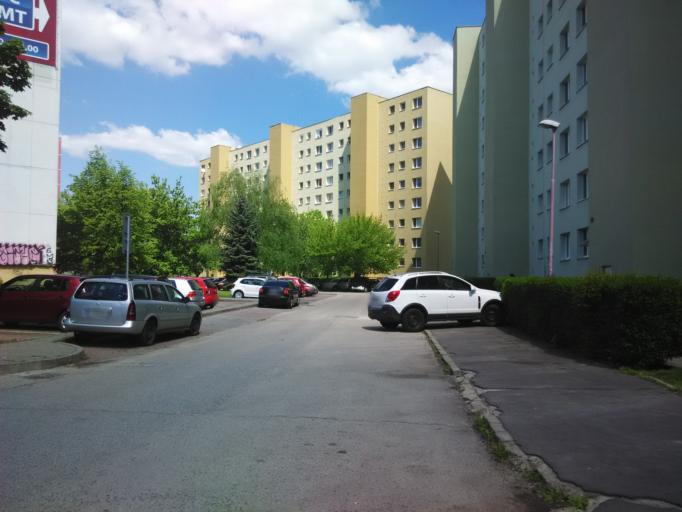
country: SK
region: Trnavsky
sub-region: Okres Trnava
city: Trnava
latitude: 48.3767
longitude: 17.5946
